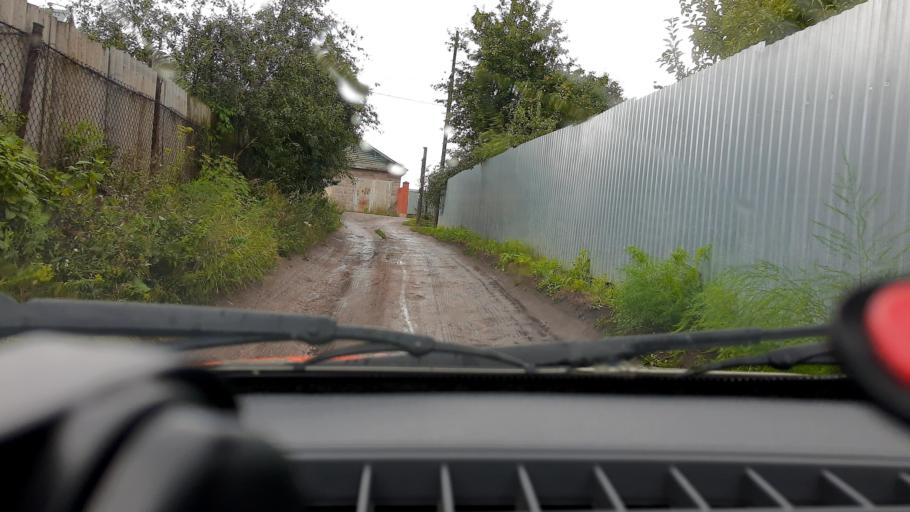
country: RU
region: Bashkortostan
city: Mikhaylovka
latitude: 54.8036
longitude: 55.7920
